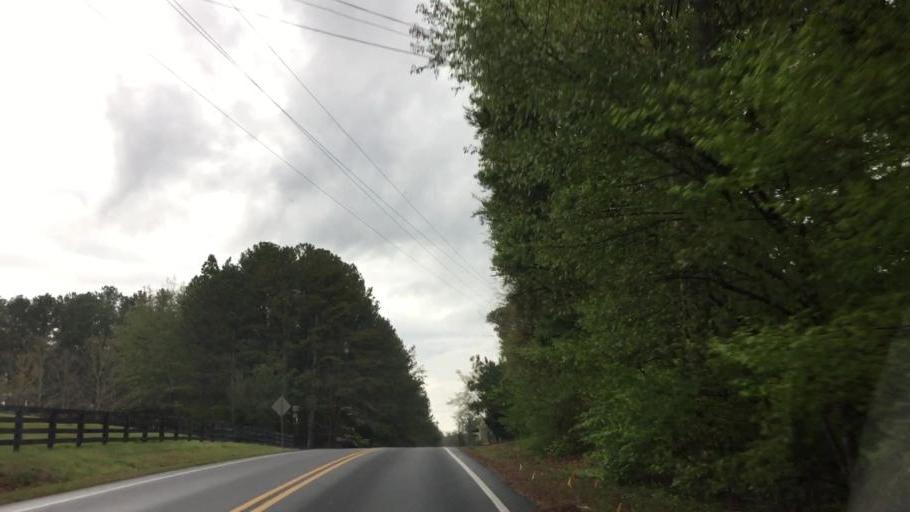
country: US
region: Georgia
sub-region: Fulton County
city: Milton
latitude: 34.1667
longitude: -84.2937
